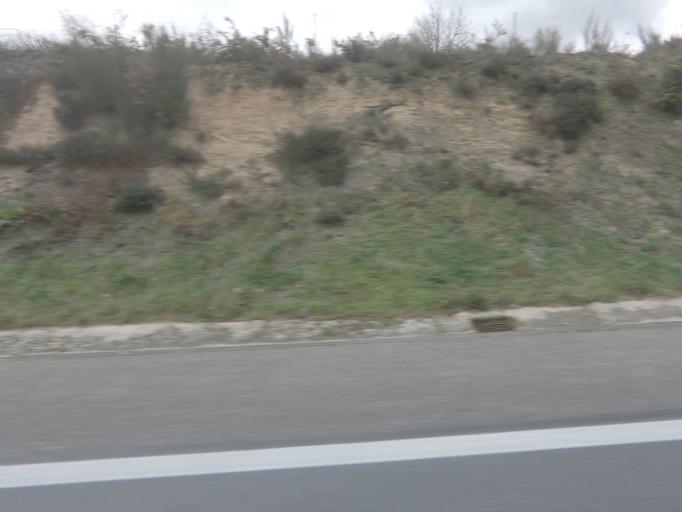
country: ES
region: Galicia
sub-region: Provincia de Ourense
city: Taboadela
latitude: 42.2695
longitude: -7.8712
